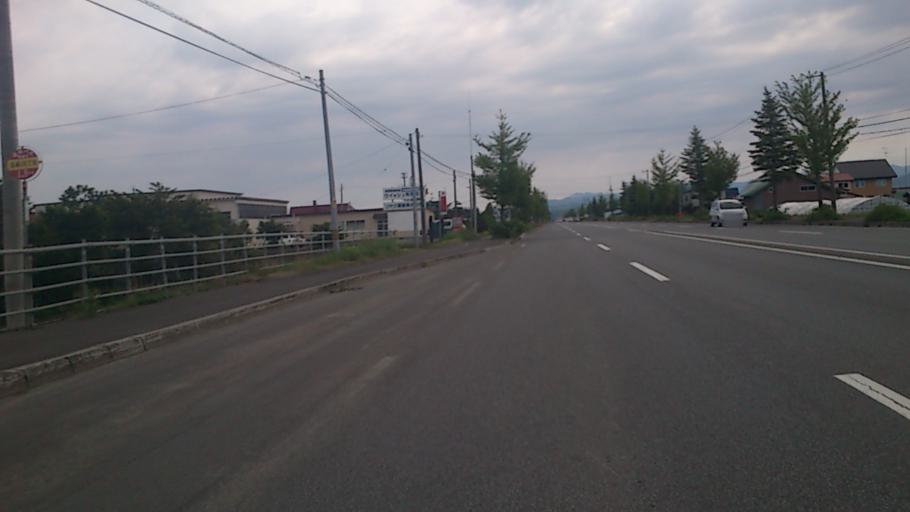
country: JP
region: Hokkaido
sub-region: Asahikawa-shi
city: Asahikawa
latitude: 43.8387
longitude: 142.4790
